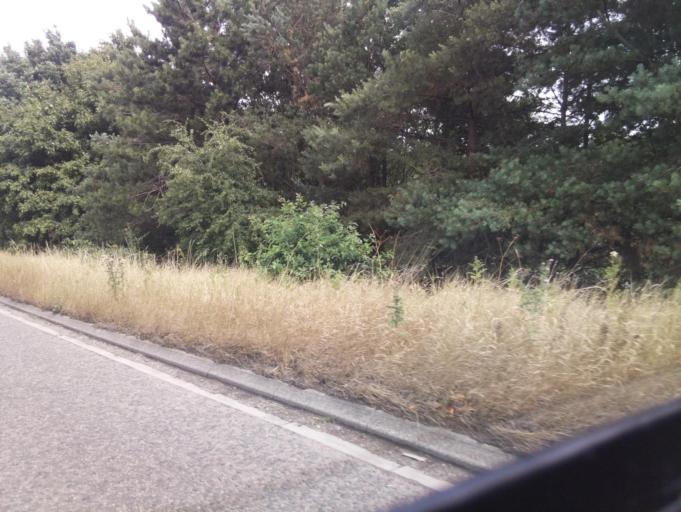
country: GB
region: England
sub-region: Derby
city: Derby
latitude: 52.9278
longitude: -1.4650
